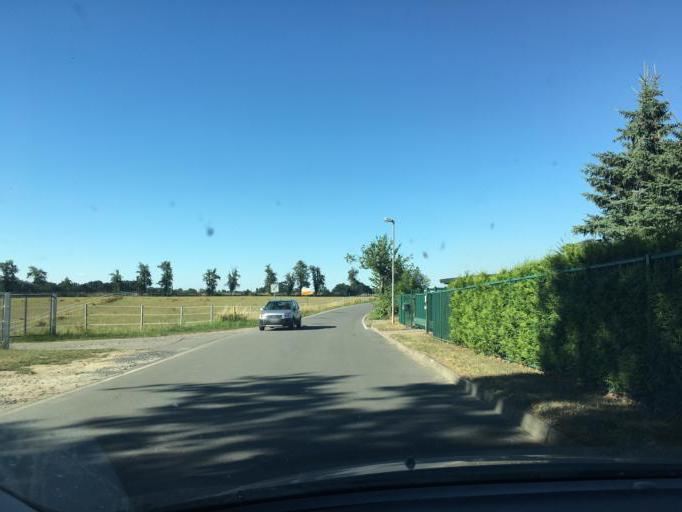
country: DE
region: Saxony
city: Frohburg
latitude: 51.0709
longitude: 12.5390
